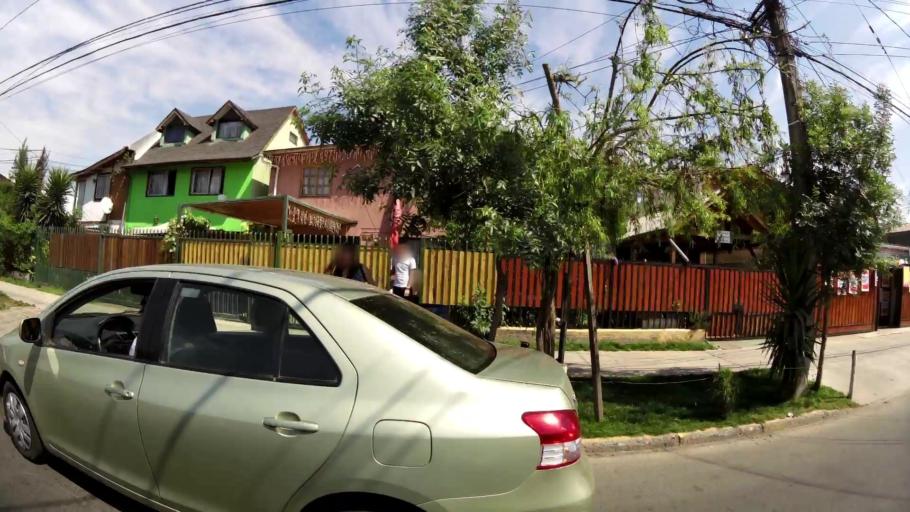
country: CL
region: Santiago Metropolitan
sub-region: Provincia de Cordillera
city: Puente Alto
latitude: -33.5901
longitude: -70.5857
